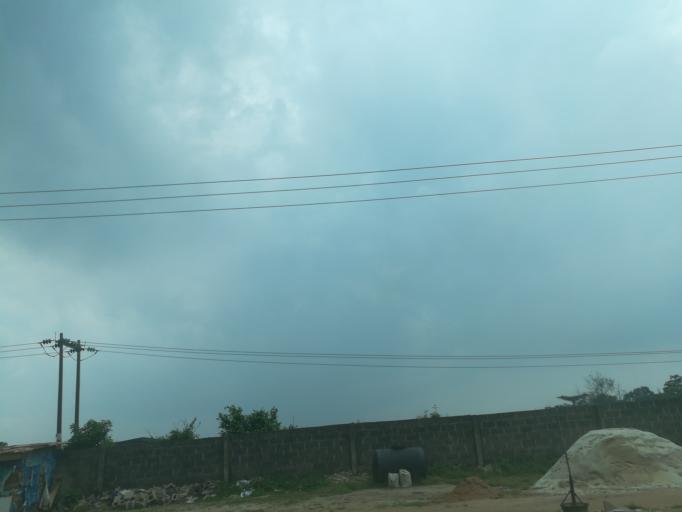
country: NG
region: Lagos
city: Ikorodu
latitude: 6.5784
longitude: 3.5905
